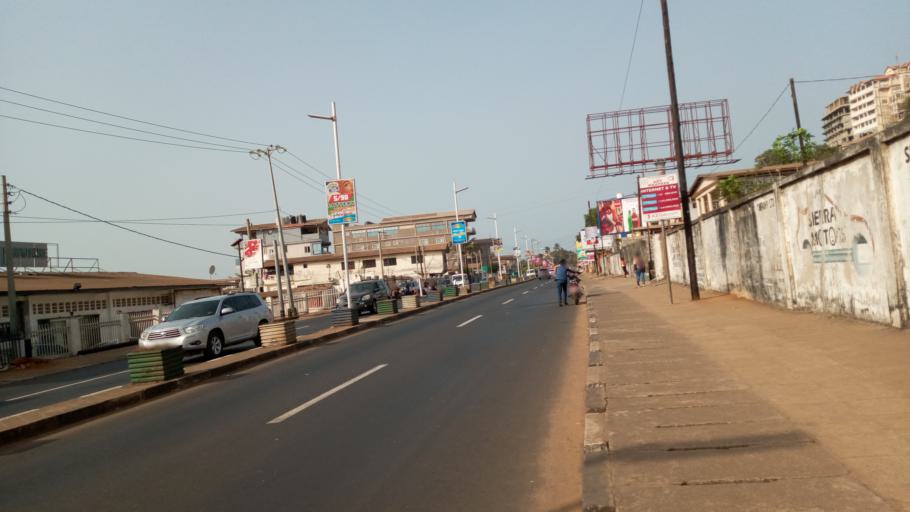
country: SL
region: Western Area
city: Freetown
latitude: 8.4813
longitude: -13.2696
